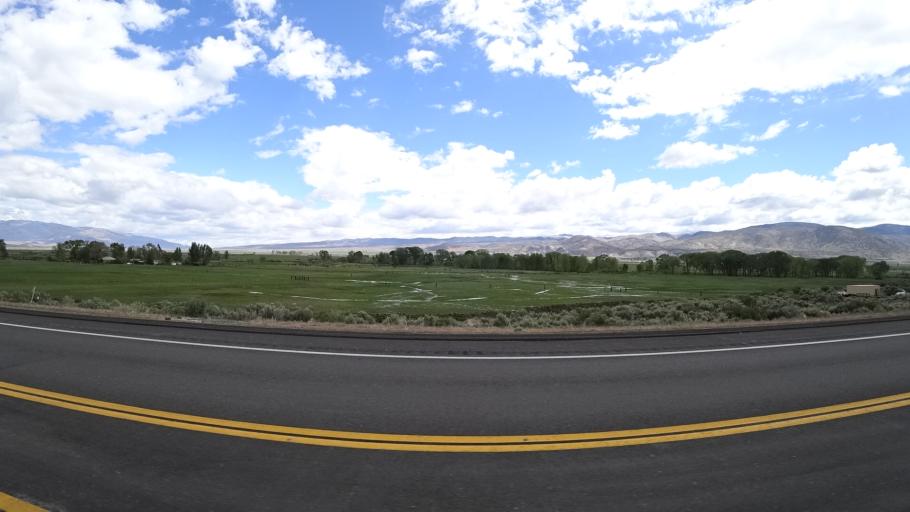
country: US
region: Nevada
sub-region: Lyon County
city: Smith Valley
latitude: 38.5885
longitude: -119.5155
